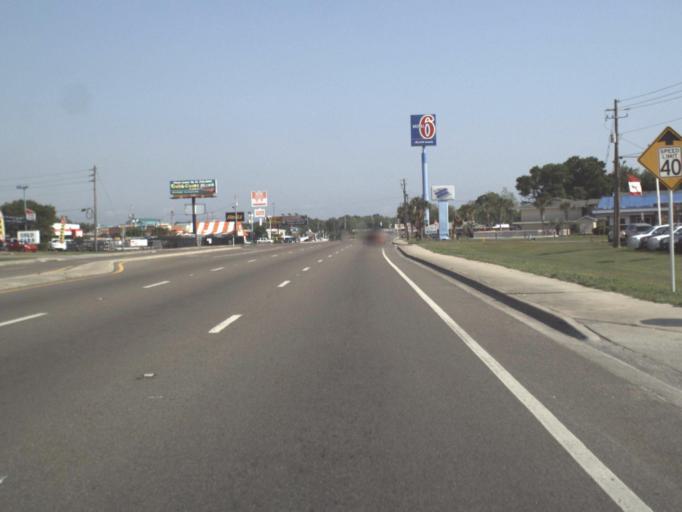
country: US
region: Florida
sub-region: Escambia County
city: Brent
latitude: 30.4730
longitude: -87.2472
